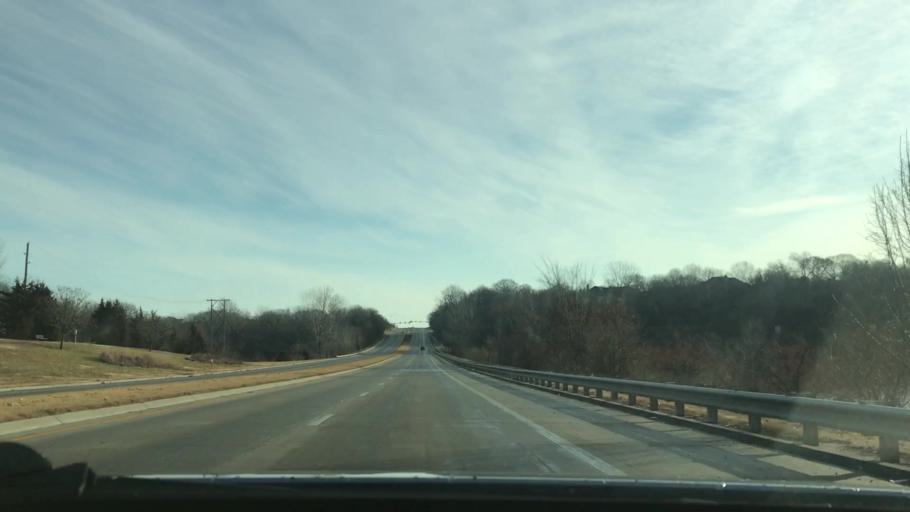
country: US
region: Missouri
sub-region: Platte County
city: Parkville
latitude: 39.2106
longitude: -94.6717
